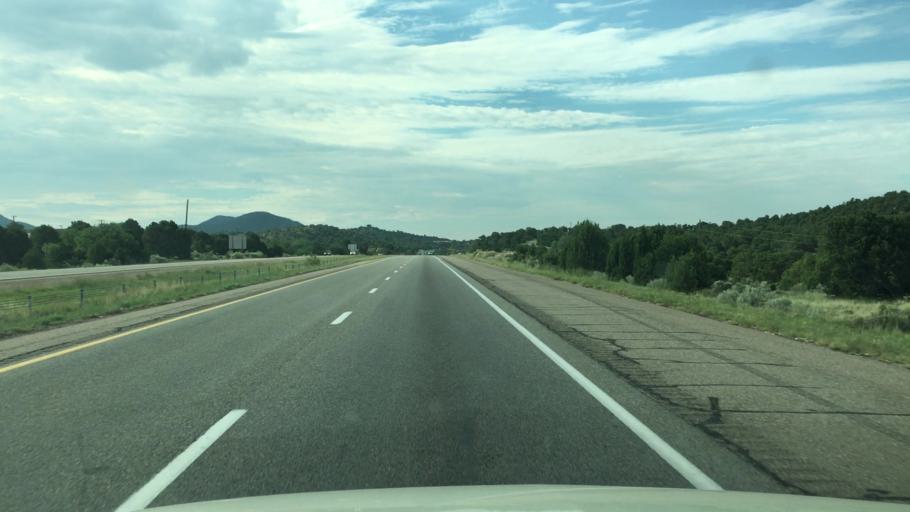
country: US
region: New Mexico
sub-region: Santa Fe County
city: Santa Fe
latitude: 35.6282
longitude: -105.9231
